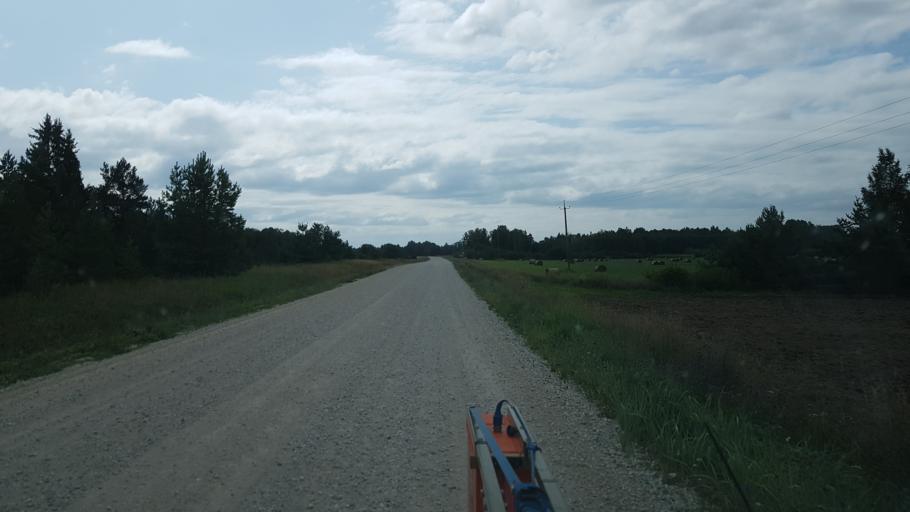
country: EE
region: Paernumaa
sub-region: Halinga vald
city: Parnu-Jaagupi
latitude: 58.5697
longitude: 24.4097
